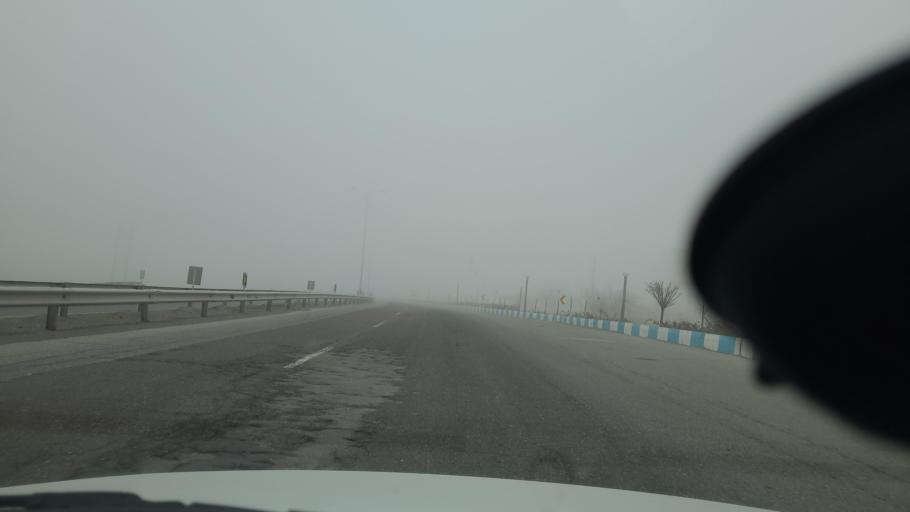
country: IR
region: Razavi Khorasan
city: Fariman
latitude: 35.7794
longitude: 59.7387
